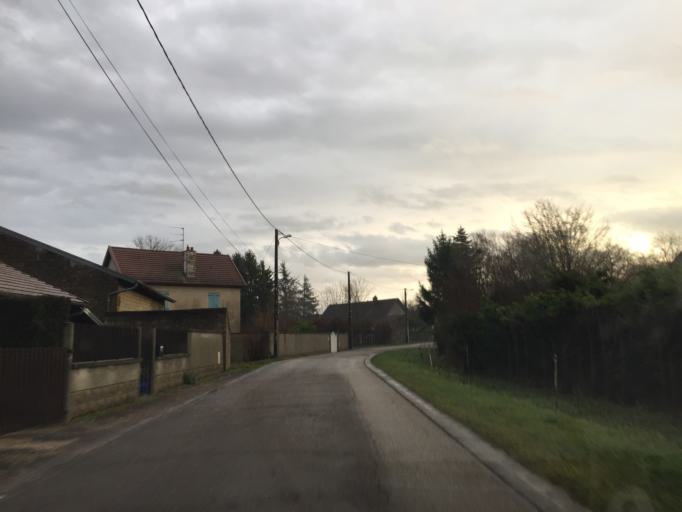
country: FR
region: Franche-Comte
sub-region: Departement du Jura
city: Choisey
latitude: 47.0189
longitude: 5.4896
